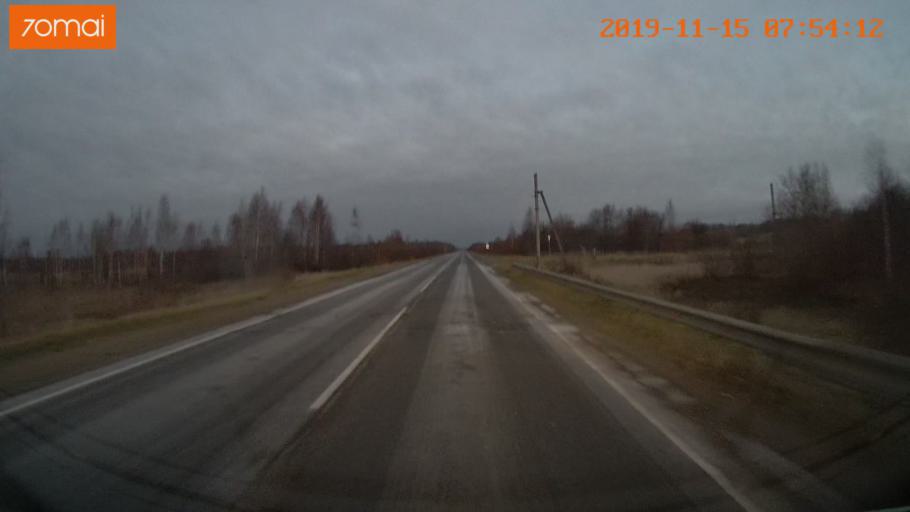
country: RU
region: Vologda
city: Cherepovets
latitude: 58.8964
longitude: 38.1785
